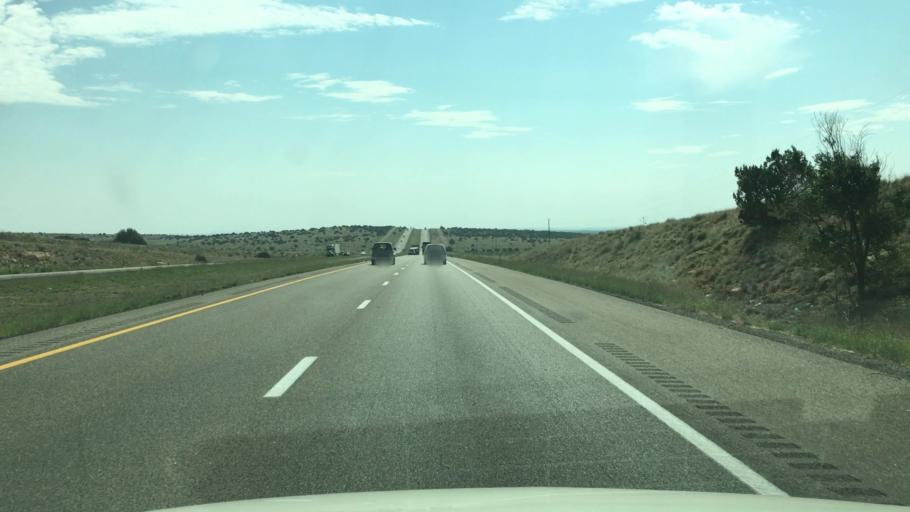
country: US
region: New Mexico
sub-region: Guadalupe County
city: Santa Rosa
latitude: 34.9720
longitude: -104.9096
